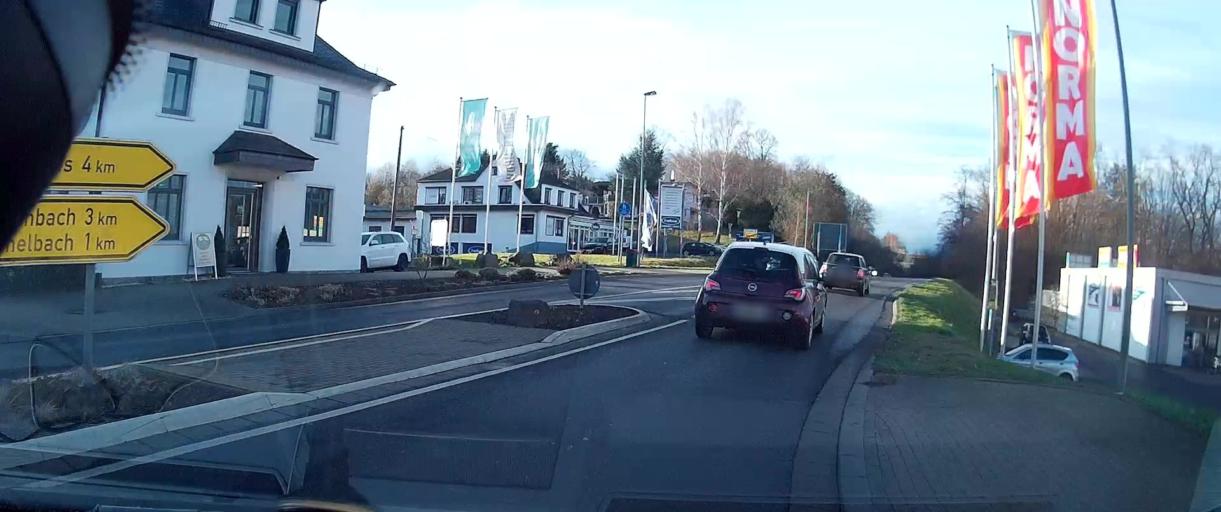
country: DE
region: Rheinland-Pfalz
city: Montabaur
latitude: 50.4421
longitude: 7.8196
